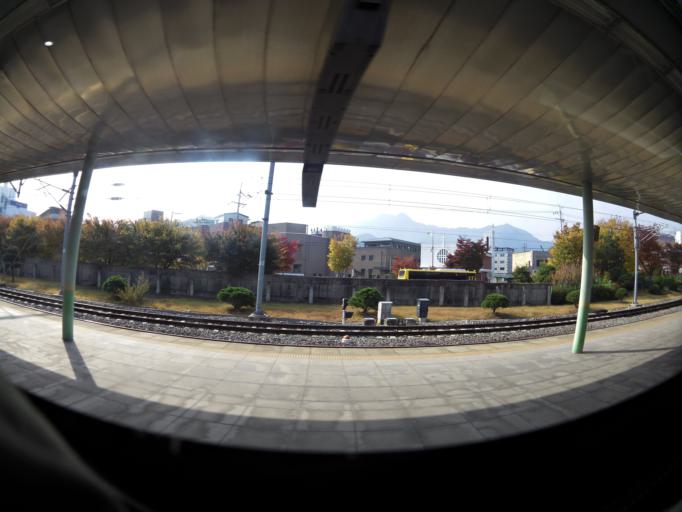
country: KR
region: Gyeongsangbuk-do
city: Gumi
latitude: 36.1271
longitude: 128.3338
